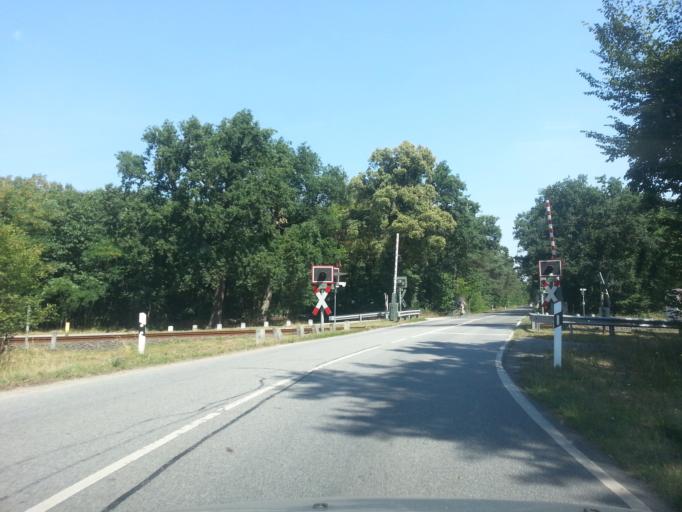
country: DE
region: Hesse
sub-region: Regierungsbezirk Darmstadt
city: Einhausen
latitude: 49.6515
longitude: 8.5365
